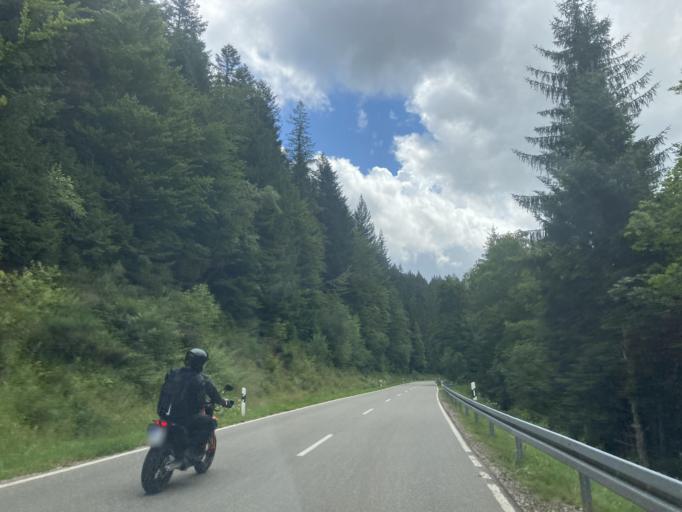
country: DE
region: Baden-Wuerttemberg
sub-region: Freiburg Region
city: Schonach im Schwarzwald
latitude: 48.1465
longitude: 8.1597
